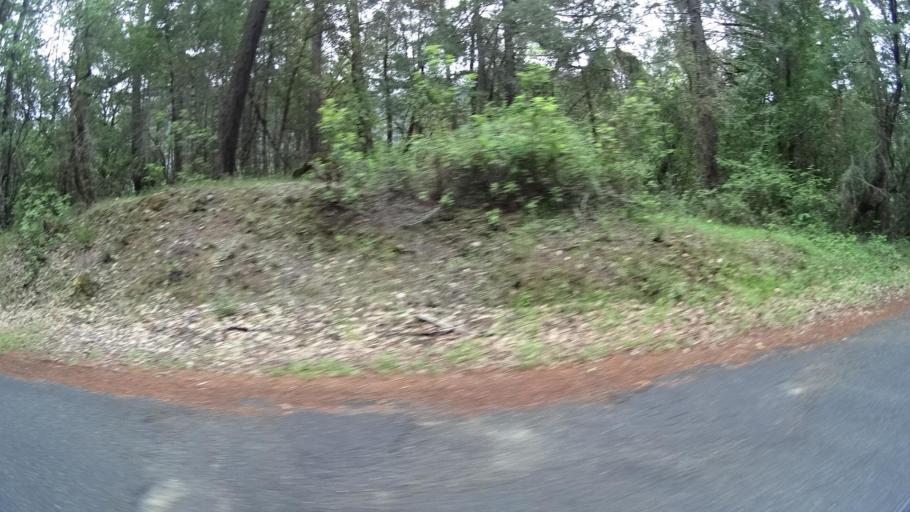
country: US
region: California
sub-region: Humboldt County
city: Willow Creek
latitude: 41.3354
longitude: -123.5195
